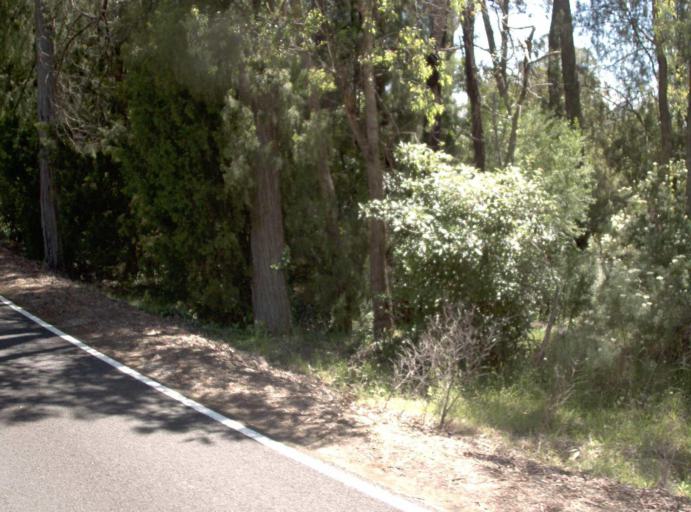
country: AU
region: Victoria
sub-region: East Gippsland
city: Lakes Entrance
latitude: -37.3534
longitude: 148.2280
